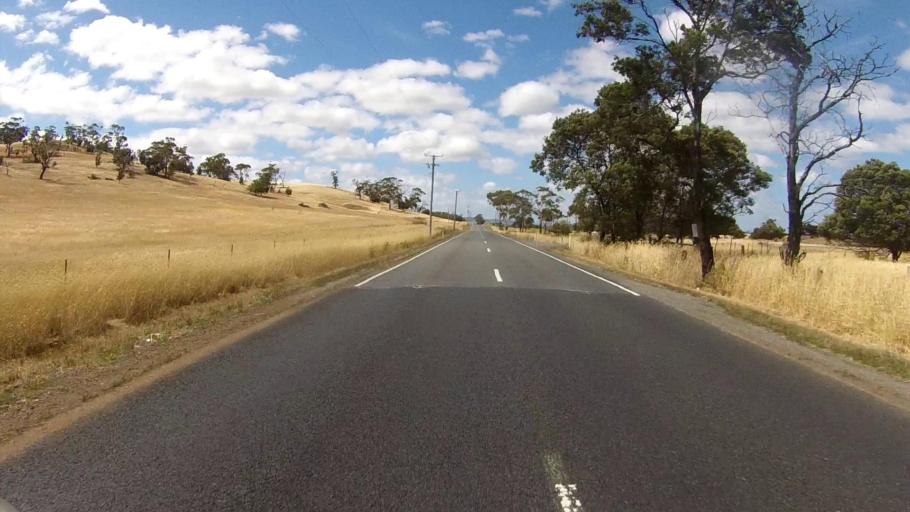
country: AU
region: Tasmania
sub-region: Sorell
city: Sorell
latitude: -42.7541
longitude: 147.5053
